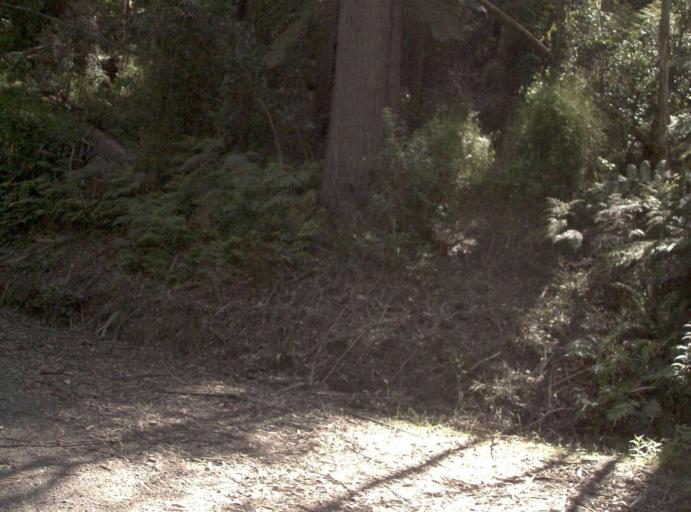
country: AU
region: New South Wales
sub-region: Bombala
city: Bombala
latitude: -37.2496
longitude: 148.7528
